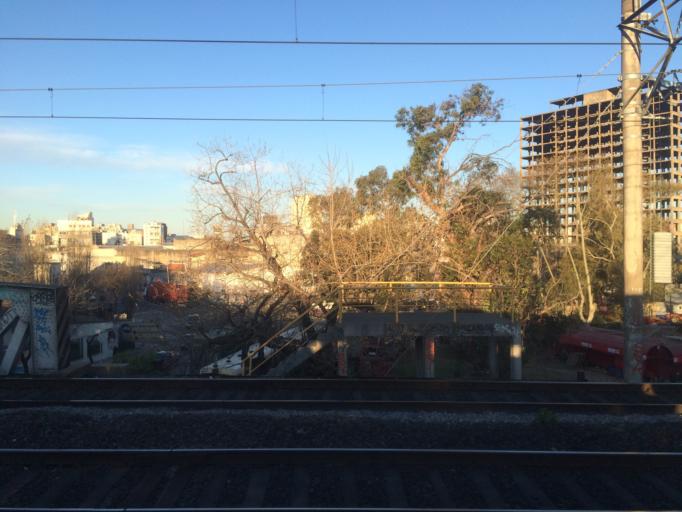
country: AR
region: Buenos Aires
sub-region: Partido de Avellaneda
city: Avellaneda
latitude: -34.6424
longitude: -58.3807
